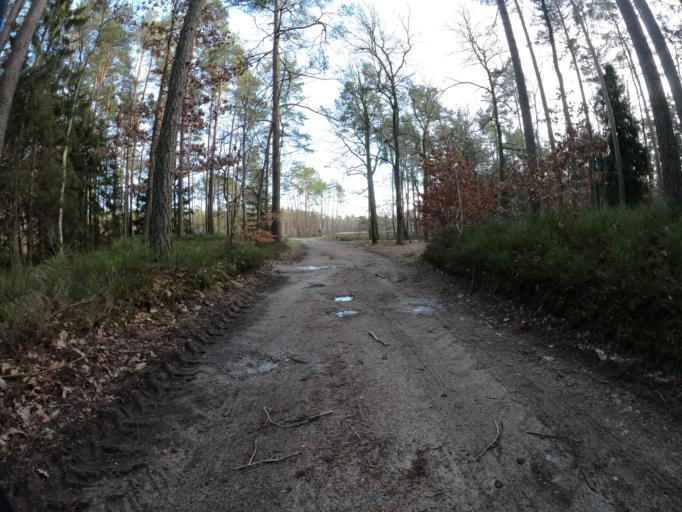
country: PL
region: West Pomeranian Voivodeship
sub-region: Powiat koszalinski
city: Polanow
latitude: 54.1716
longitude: 16.6600
